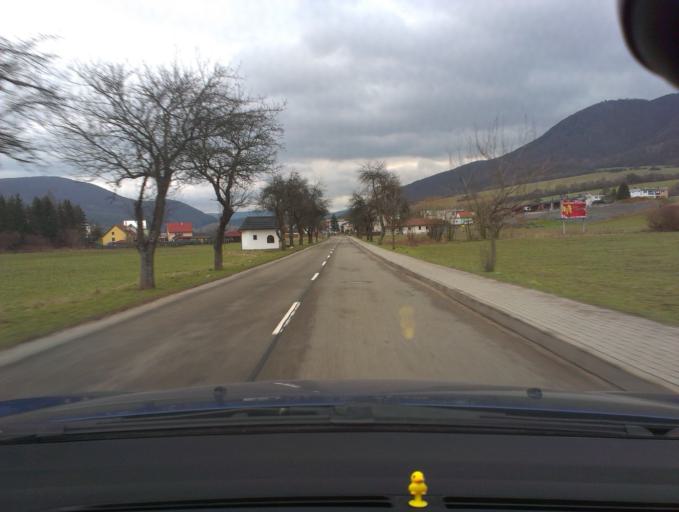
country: SK
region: Nitriansky
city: Trencianske Teplice
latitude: 48.8973
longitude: 18.2096
